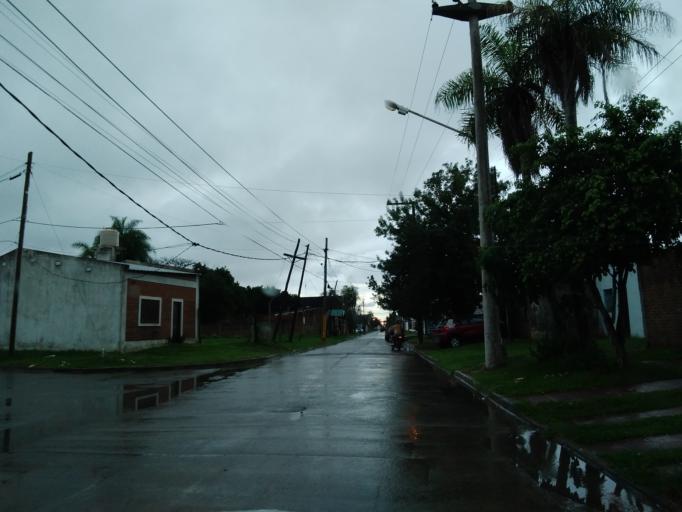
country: AR
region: Corrientes
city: Corrientes
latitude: -27.4974
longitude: -58.8209
